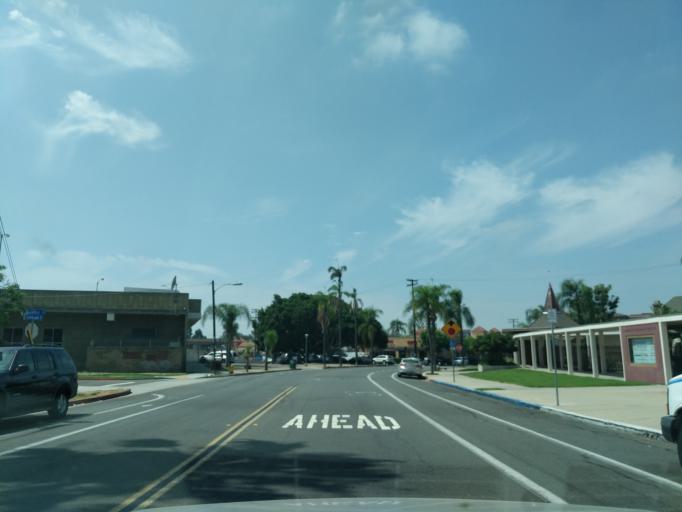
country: US
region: California
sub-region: San Diego County
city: San Diego
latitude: 32.7501
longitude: -117.1504
